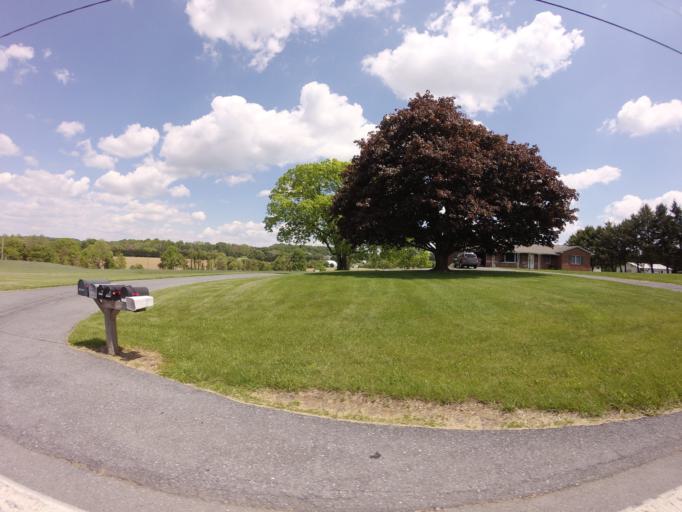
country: US
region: Maryland
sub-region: Frederick County
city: Green Valley
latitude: 39.3009
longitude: -77.3038
